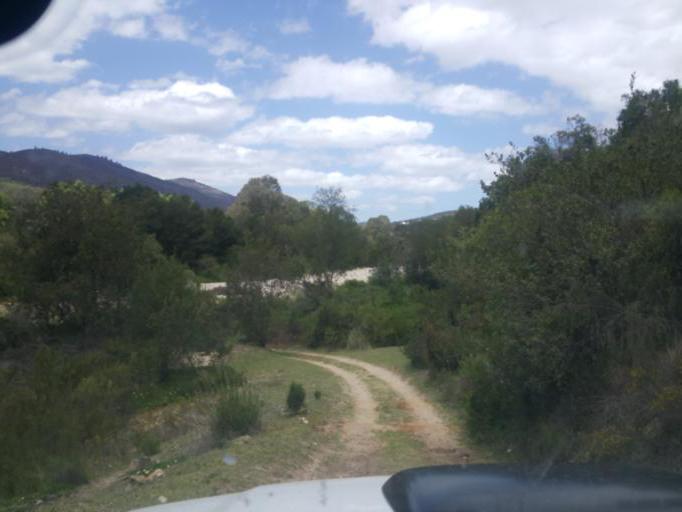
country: ZA
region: Western Cape
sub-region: Eden District Municipality
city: Knysna
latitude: -33.8217
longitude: 23.1811
